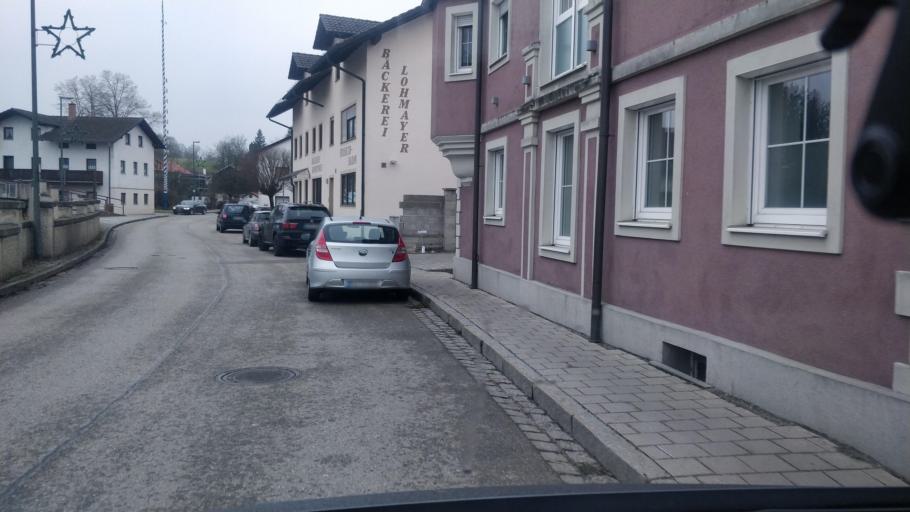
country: DE
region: Bavaria
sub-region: Upper Bavaria
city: Schwindegg
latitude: 48.2721
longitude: 12.2570
